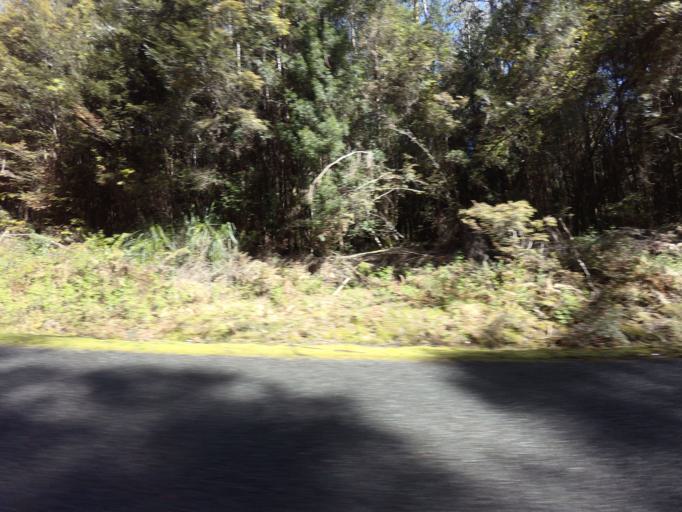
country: AU
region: Tasmania
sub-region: Derwent Valley
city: New Norfolk
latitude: -42.7455
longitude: 146.4146
